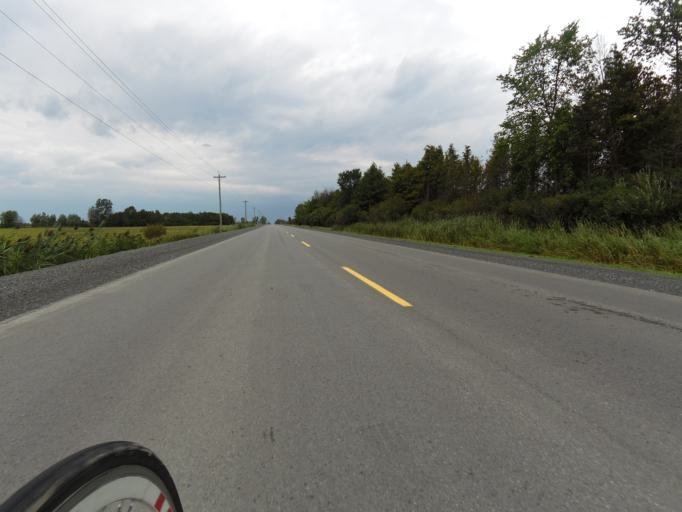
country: CA
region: Ontario
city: Bells Corners
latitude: 45.2210
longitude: -75.7746
